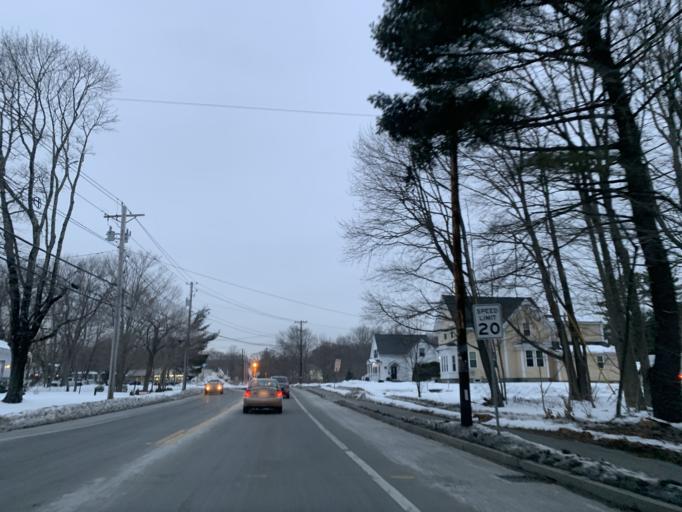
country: US
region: Massachusetts
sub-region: Norfolk County
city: Stoughton
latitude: 42.1194
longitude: -71.0858
